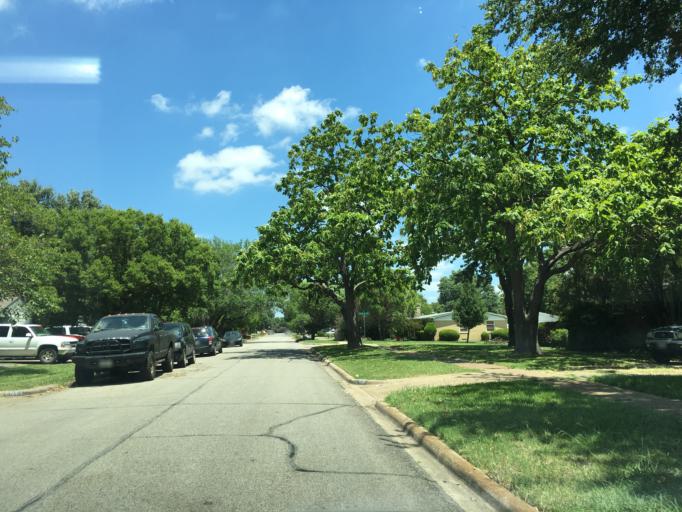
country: US
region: Texas
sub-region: Dallas County
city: Garland
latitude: 32.8371
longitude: -96.6659
